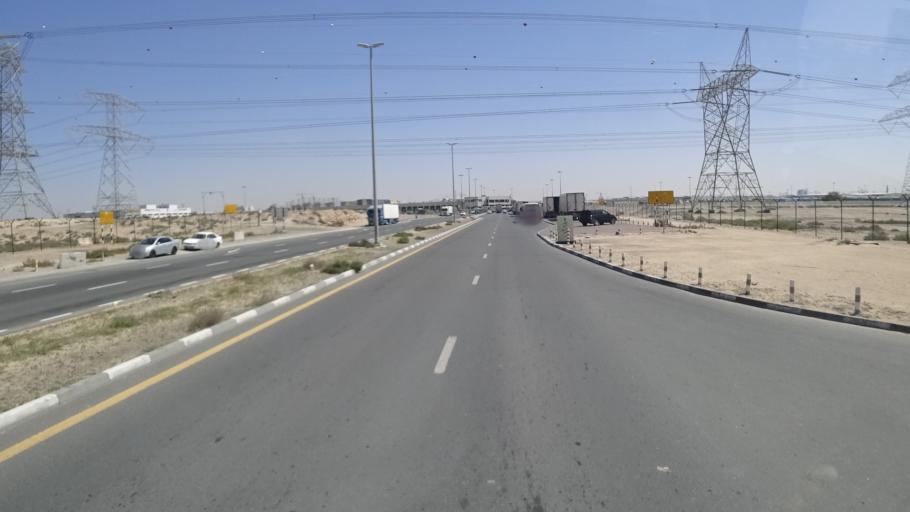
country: AE
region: Ash Shariqah
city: Sharjah
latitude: 25.1739
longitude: 55.3816
